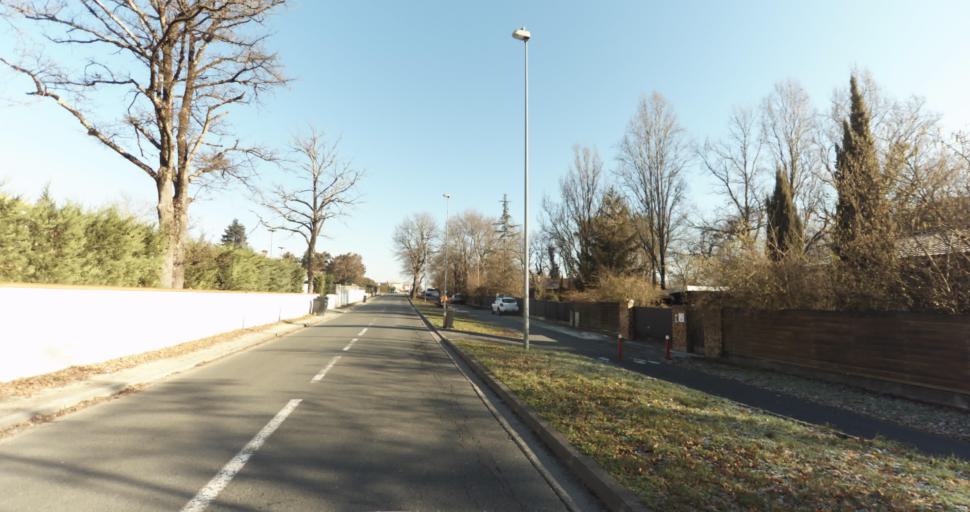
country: FR
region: Aquitaine
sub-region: Departement de la Gironde
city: Carbon-Blanc
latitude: 44.8884
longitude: -0.5108
